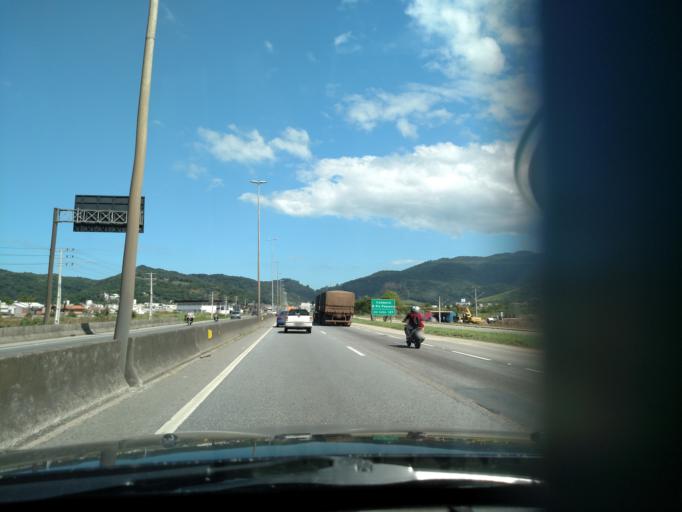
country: BR
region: Santa Catarina
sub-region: Balneario Camboriu
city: Balneario Camboriu
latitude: -27.0144
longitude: -48.6126
